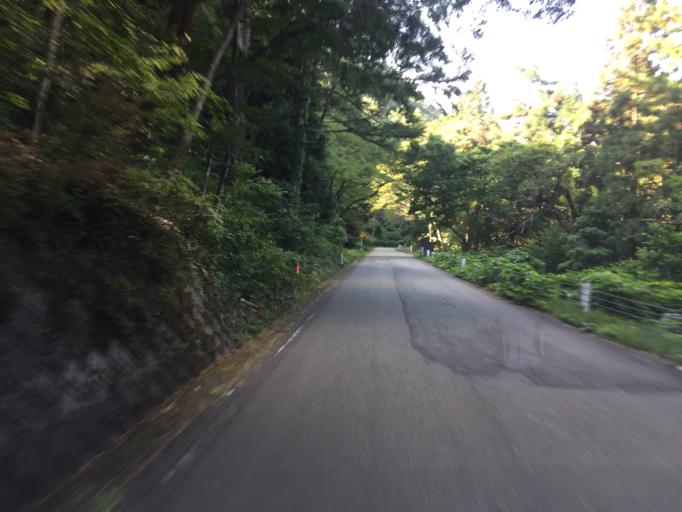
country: JP
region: Fukushima
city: Inawashiro
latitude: 37.4850
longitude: 139.9622
